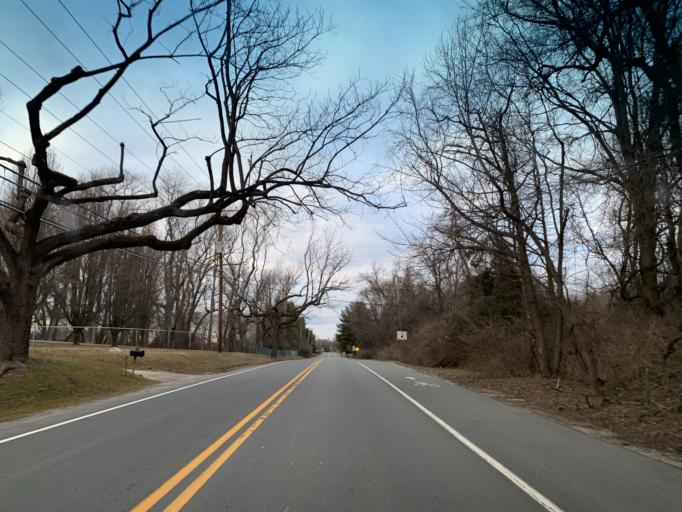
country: US
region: Delaware
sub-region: New Castle County
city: Bear
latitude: 39.5995
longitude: -75.6631
